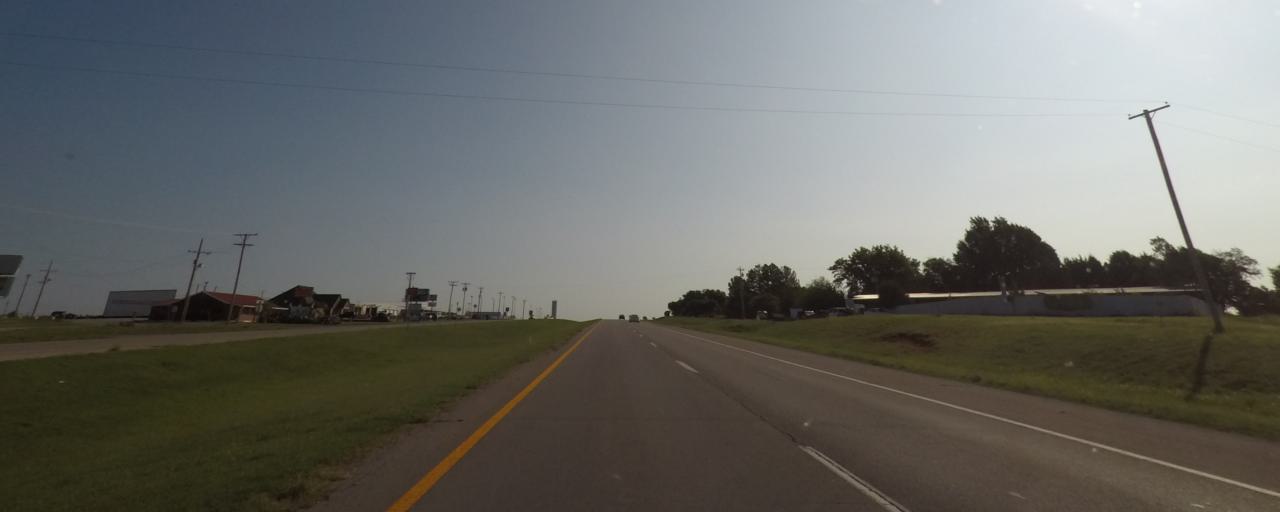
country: US
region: Oklahoma
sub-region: McClain County
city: Blanchard
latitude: 35.1460
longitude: -97.6412
